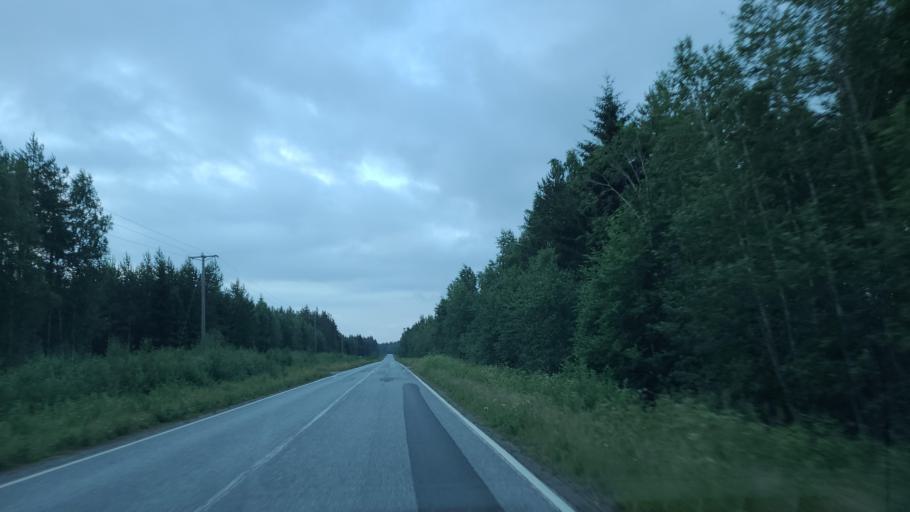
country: FI
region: Ostrobothnia
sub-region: Vaasa
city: Replot
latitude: 63.2204
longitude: 21.2458
